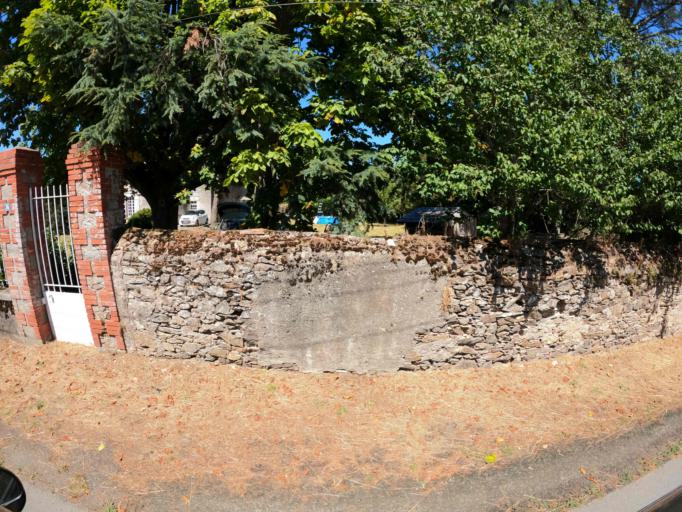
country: FR
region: Pays de la Loire
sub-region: Departement de la Loire-Atlantique
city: La Limouziniere
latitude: 46.9532
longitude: -1.6068
